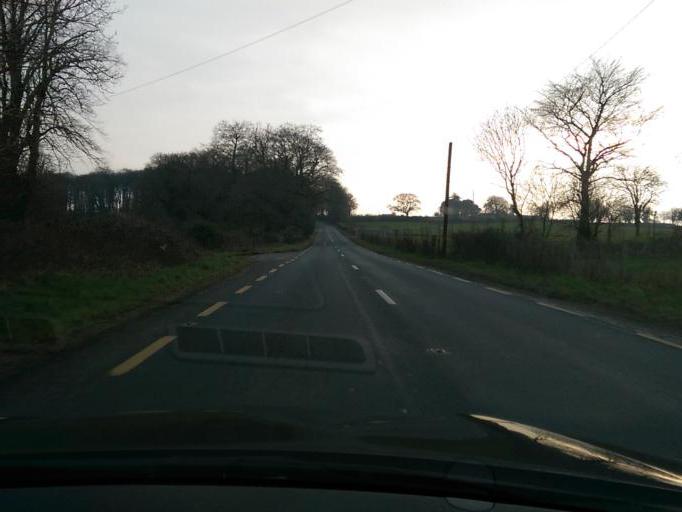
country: IE
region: Leinster
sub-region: An Longfort
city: Ballymahon
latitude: 53.5036
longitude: -7.8393
